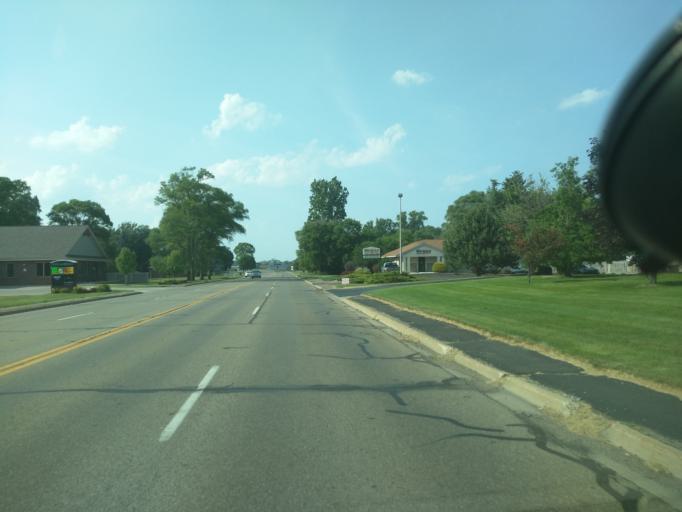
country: US
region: Michigan
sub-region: Jackson County
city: Jackson
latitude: 42.2577
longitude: -84.4477
